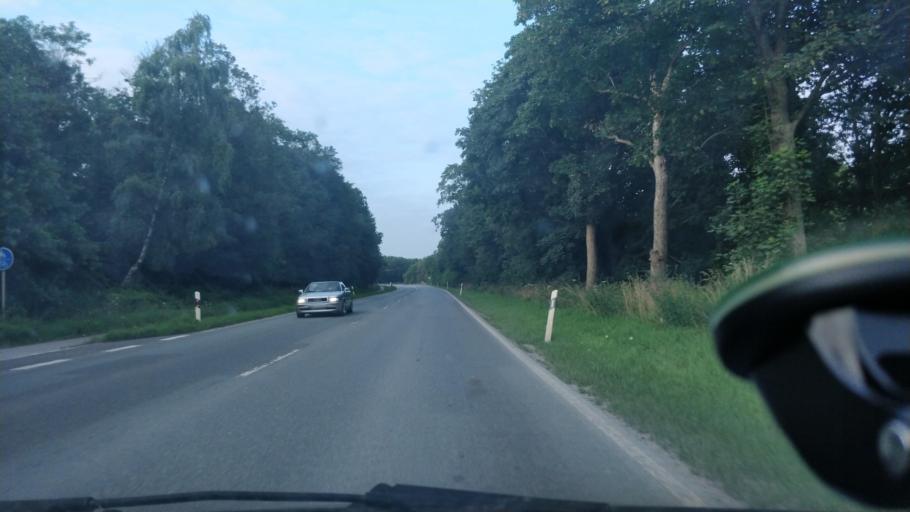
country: DE
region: North Rhine-Westphalia
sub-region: Regierungsbezirk Dusseldorf
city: Kamp-Lintfort
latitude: 51.5260
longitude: 6.5635
